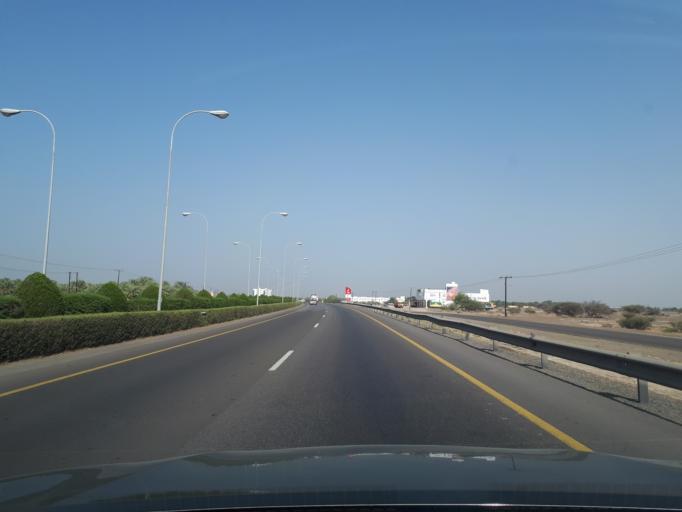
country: OM
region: Al Batinah
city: Al Sohar
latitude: 24.4124
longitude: 56.6351
